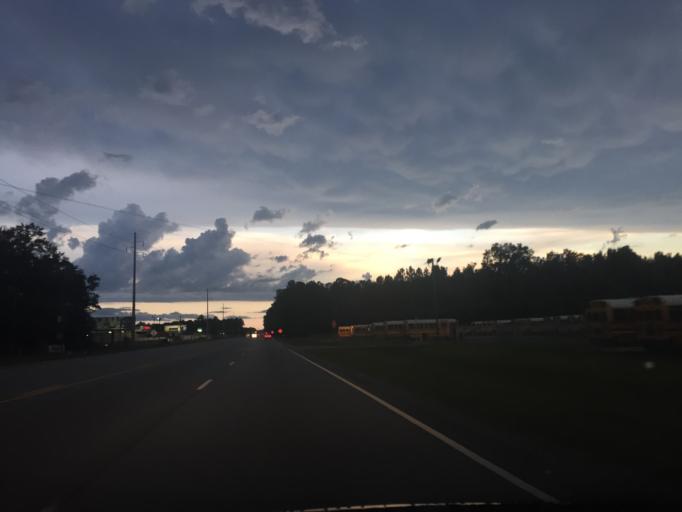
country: US
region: Georgia
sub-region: Liberty County
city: Hinesville
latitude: 31.8361
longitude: -81.5363
